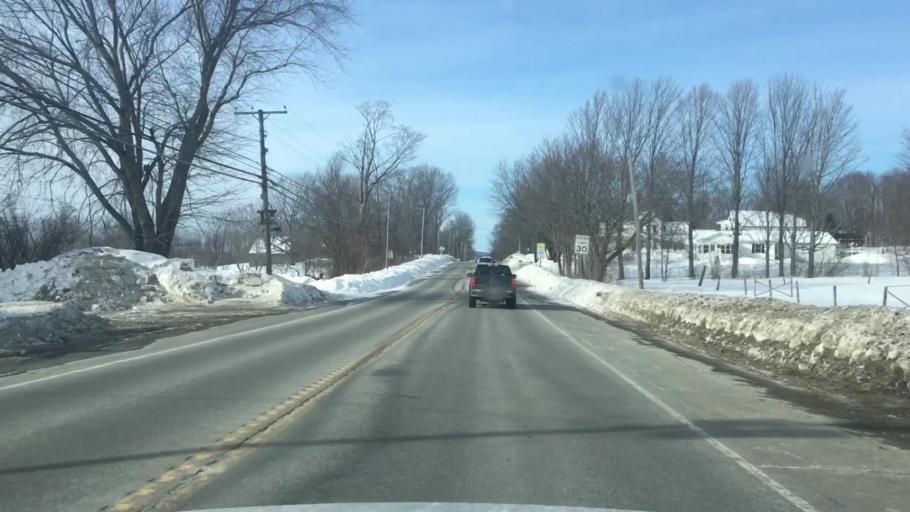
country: US
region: Maine
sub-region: Penobscot County
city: Charleston
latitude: 44.9944
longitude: -69.0192
